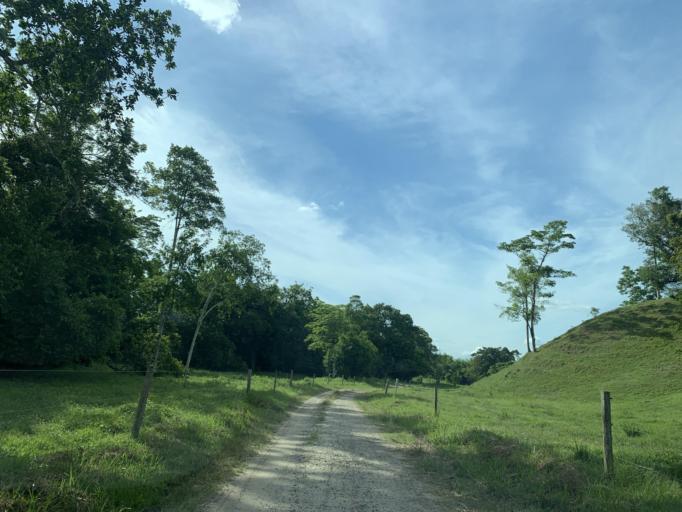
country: CO
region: Boyaca
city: Puerto Boyaca
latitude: 6.0120
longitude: -74.3942
